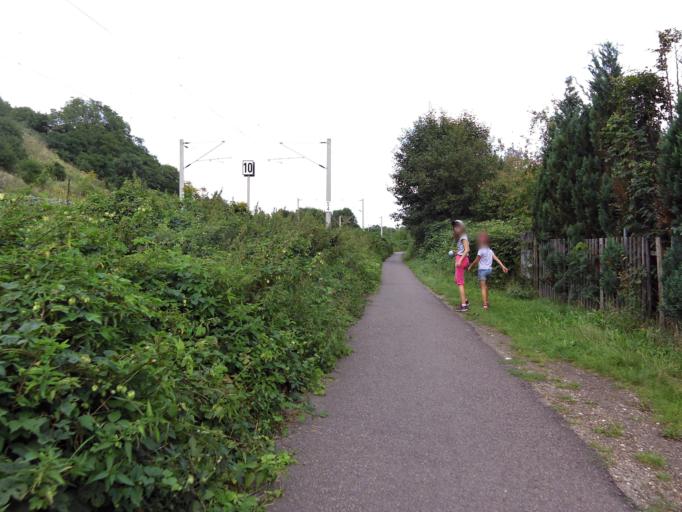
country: DE
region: Saxony
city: Leipzig
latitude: 51.3602
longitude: 12.3312
